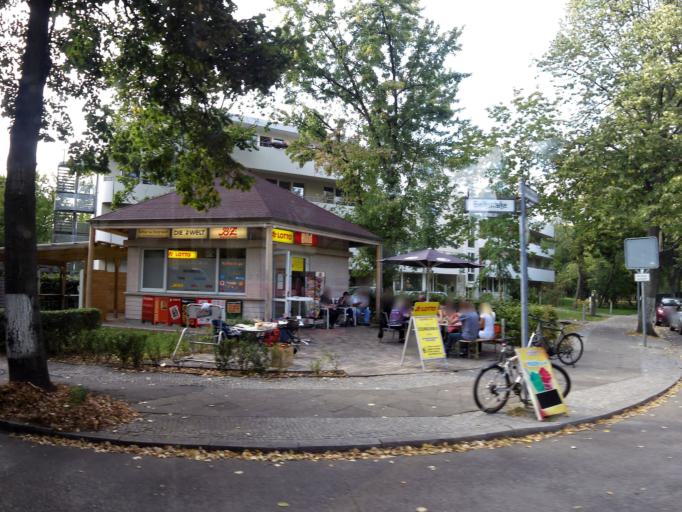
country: DE
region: Berlin
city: Marienfelde
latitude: 52.4294
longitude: 13.3588
